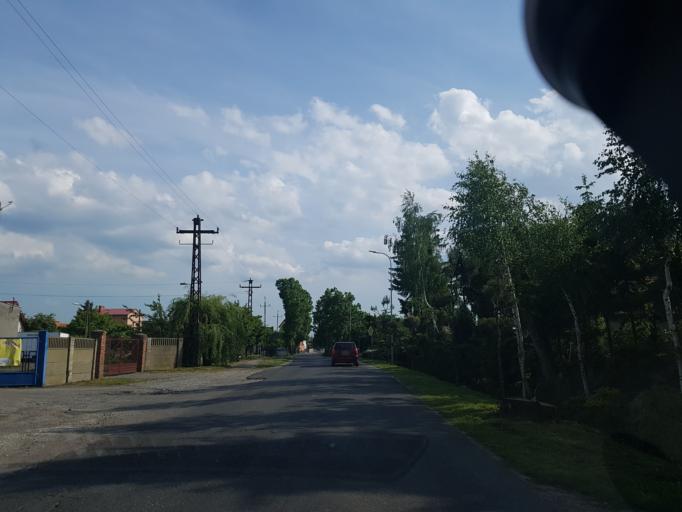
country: PL
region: Lower Silesian Voivodeship
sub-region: Powiat olawski
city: Wierzbno
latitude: 50.8965
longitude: 17.1308
